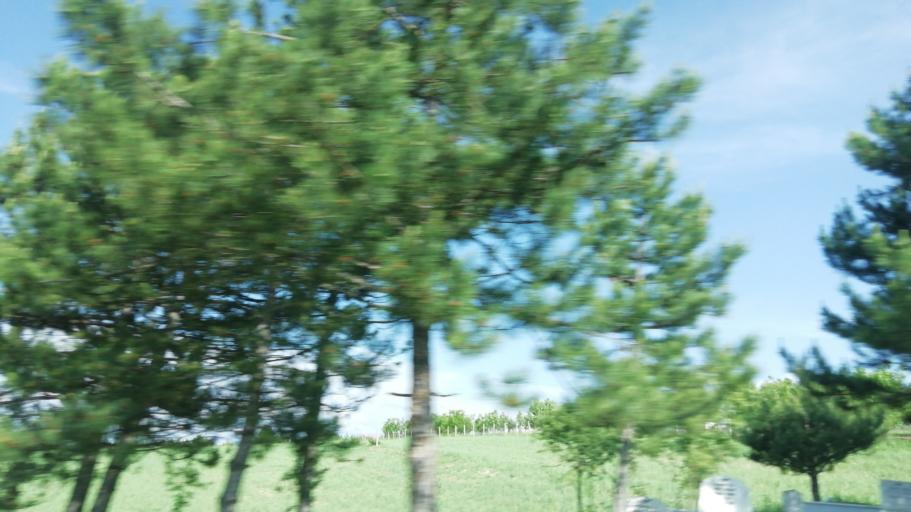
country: TR
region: Karabuk
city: Karabuk
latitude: 41.0907
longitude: 32.5880
